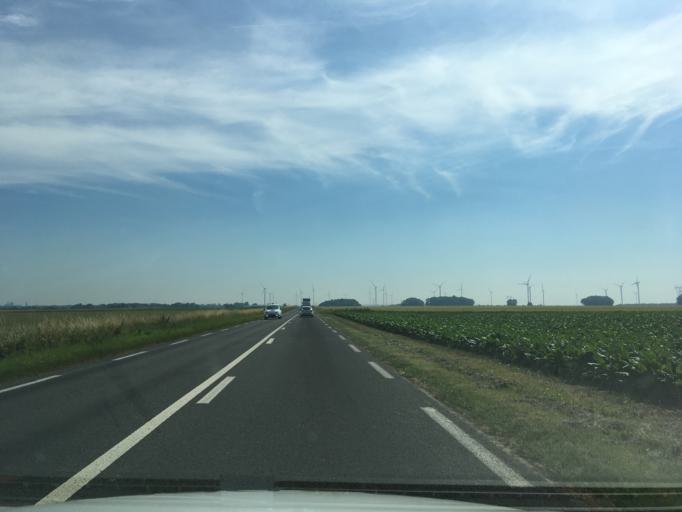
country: FR
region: Picardie
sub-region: Departement de la Somme
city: Roye
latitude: 49.6642
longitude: 2.7355
